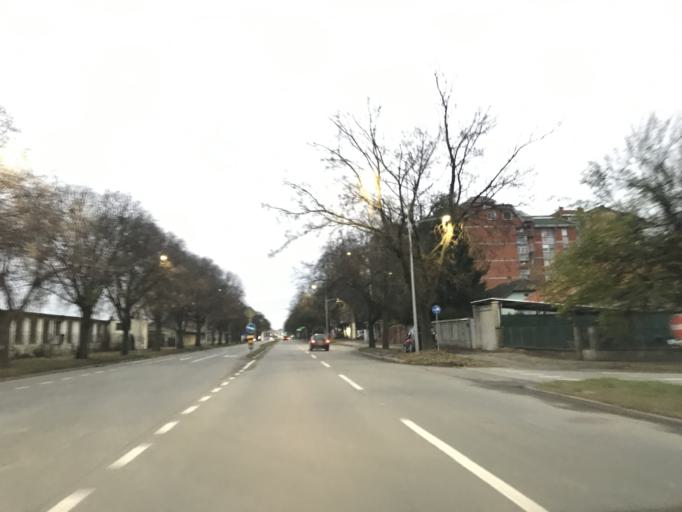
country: RS
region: Autonomna Pokrajina Vojvodina
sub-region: Juznobacki Okrug
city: Novi Sad
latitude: 45.2707
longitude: 19.8083
